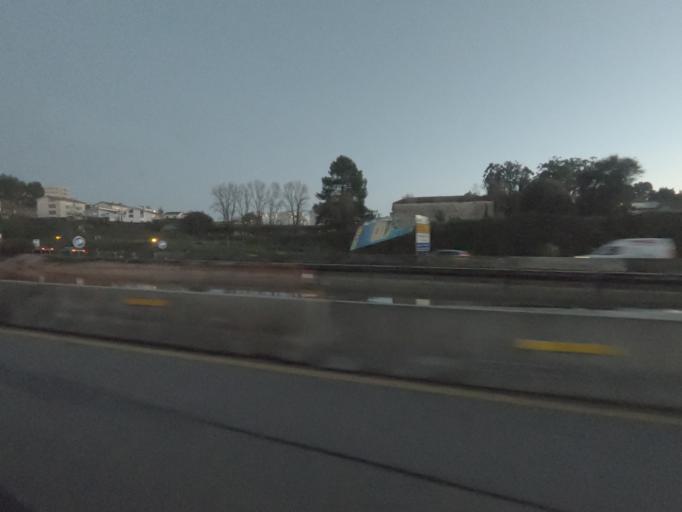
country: PT
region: Porto
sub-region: Maia
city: Pedroucos
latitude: 41.1993
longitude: -8.5814
